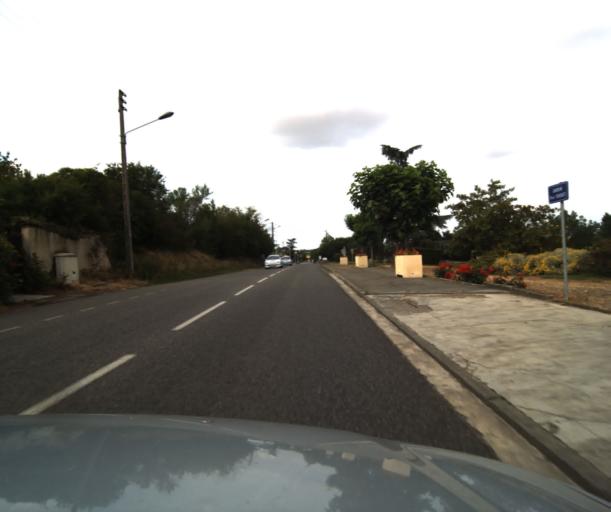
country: FR
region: Midi-Pyrenees
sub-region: Departement du Tarn-et-Garonne
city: Beaumont-de-Lomagne
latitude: 43.8846
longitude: 0.9944
